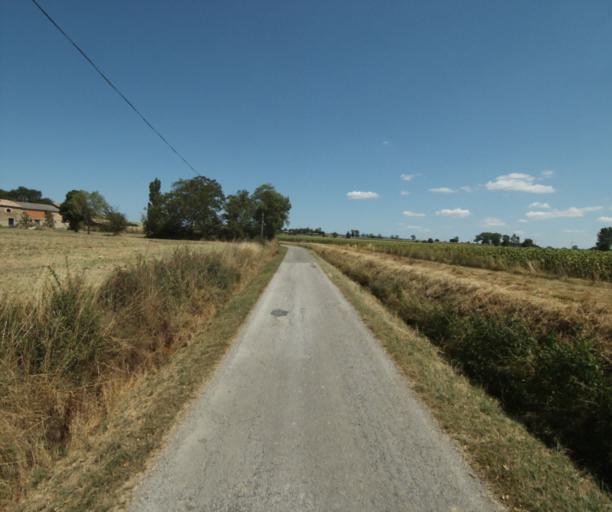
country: FR
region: Midi-Pyrenees
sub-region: Departement de la Haute-Garonne
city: Saint-Felix-Lauragais
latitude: 43.4845
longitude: 1.8849
